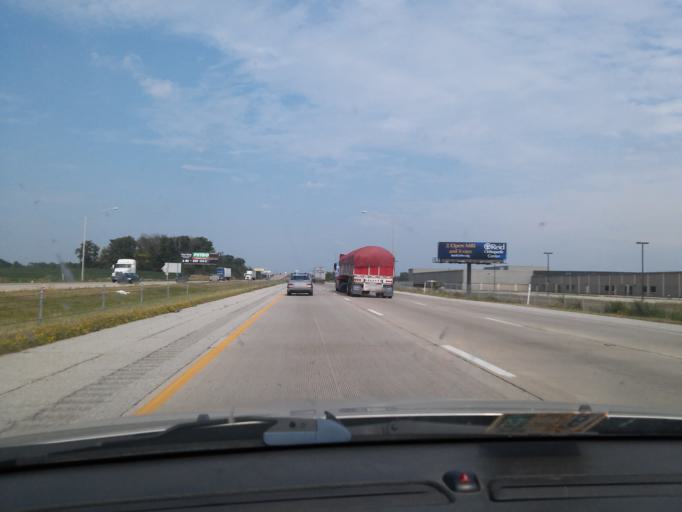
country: US
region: Indiana
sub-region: Wayne County
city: Richmond
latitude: 39.8682
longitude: -84.9203
